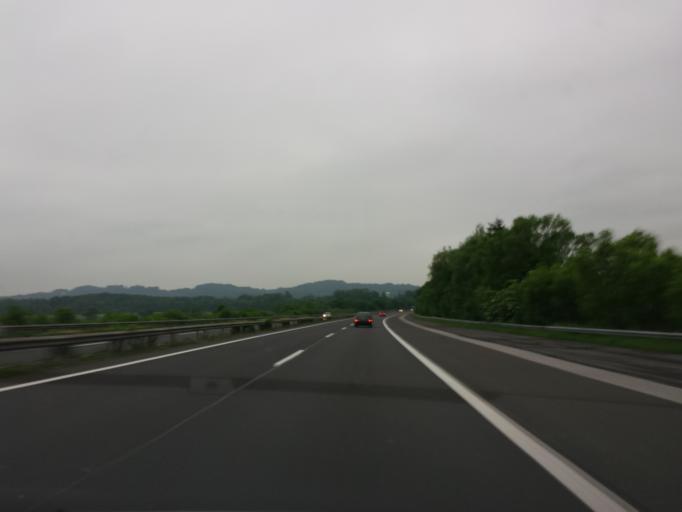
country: AT
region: Styria
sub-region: Politischer Bezirk Hartberg-Fuerstenfeld
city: Hainersdorf
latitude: 47.0921
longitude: 15.9794
